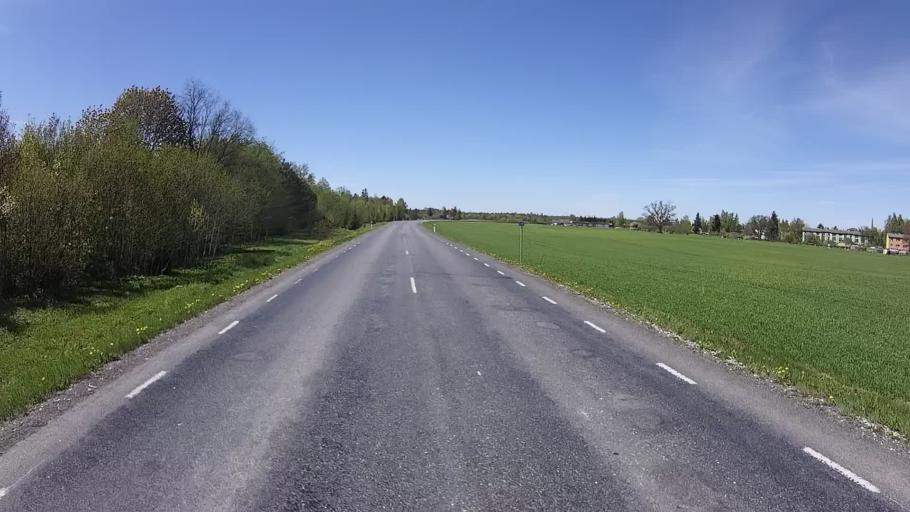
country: EE
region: Raplamaa
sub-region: Kehtna vald
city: Kehtna
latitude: 59.0542
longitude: 24.9618
